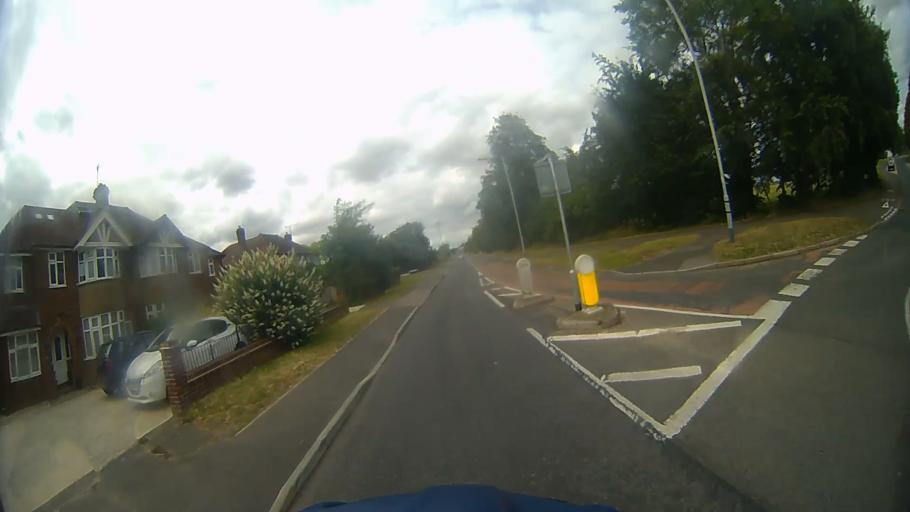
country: GB
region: England
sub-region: Wokingham
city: Earley
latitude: 51.4508
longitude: -0.9271
